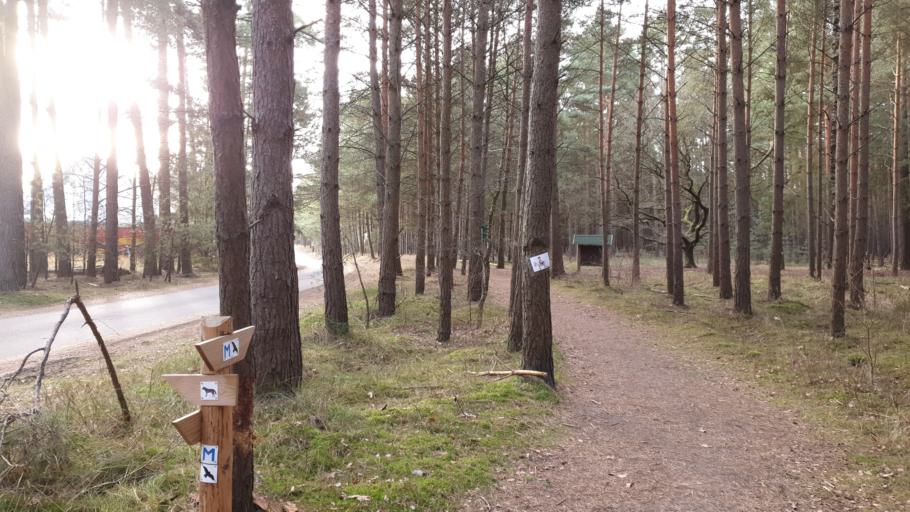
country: DE
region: Mecklenburg-Vorpommern
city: Wesenberg
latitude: 53.3023
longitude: 12.9332
